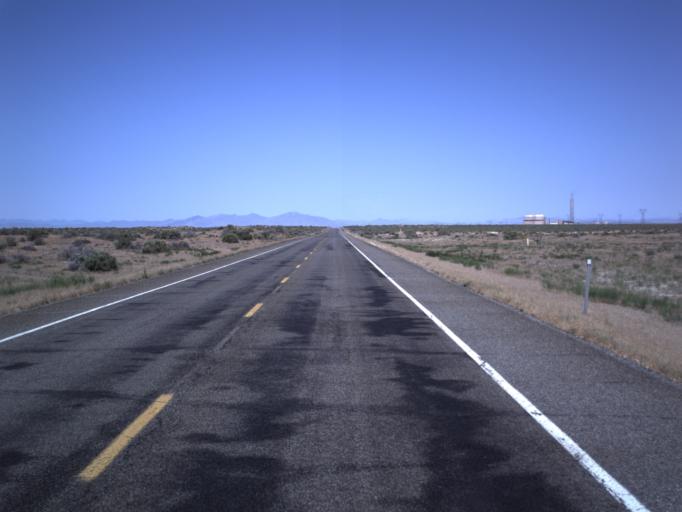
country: US
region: Utah
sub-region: Millard County
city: Delta
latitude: 39.4809
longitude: -112.5115
